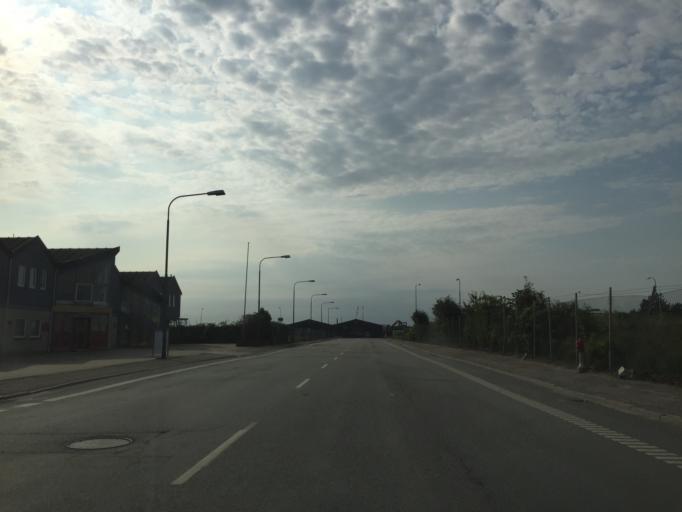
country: DK
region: Capital Region
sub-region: Gentofte Kommune
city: Charlottenlund
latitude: 55.7175
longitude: 12.6008
